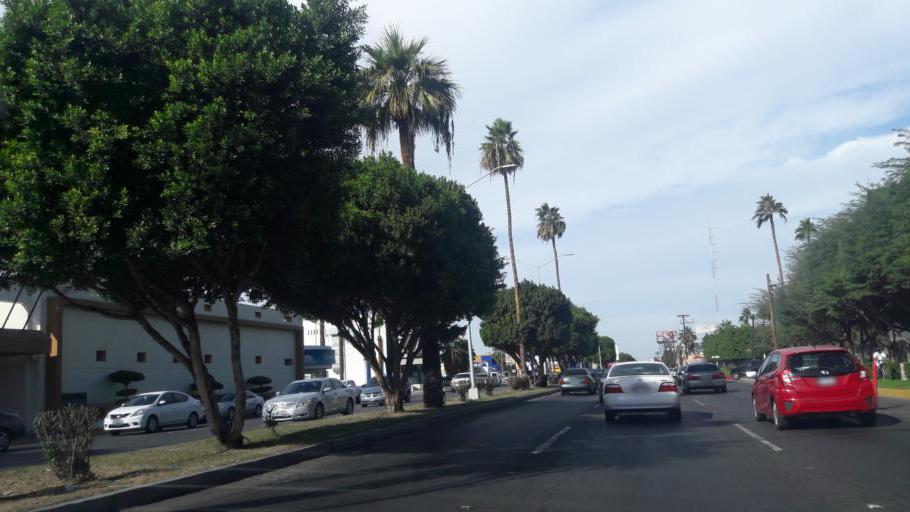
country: MX
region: Baja California
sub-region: Mexicali
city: Mexicali
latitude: 32.6383
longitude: -115.4488
